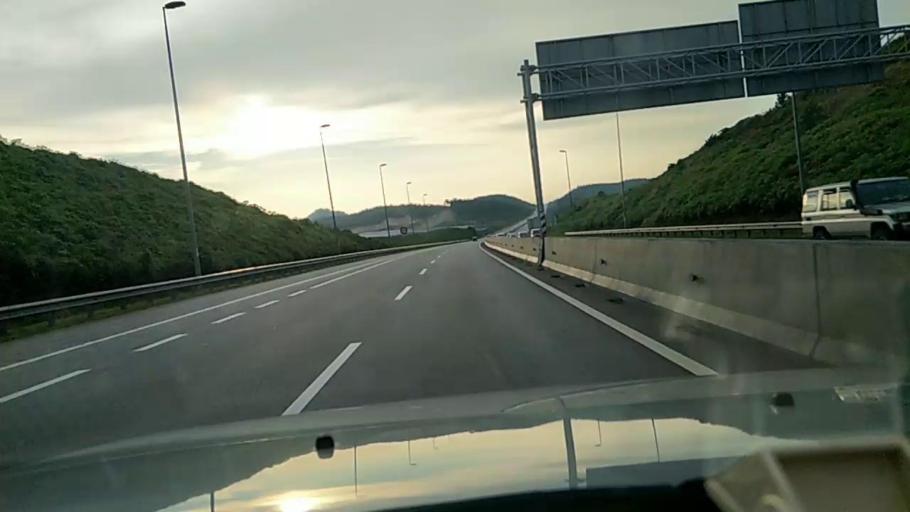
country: MY
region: Selangor
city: Batu Arang
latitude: 3.2739
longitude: 101.4581
